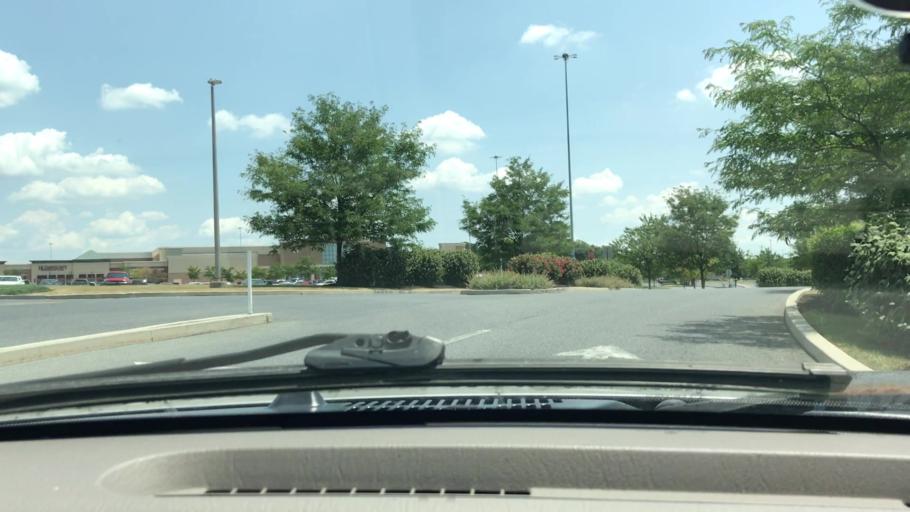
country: US
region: Pennsylvania
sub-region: Lancaster County
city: East Petersburg
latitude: 40.0667
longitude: -76.3430
